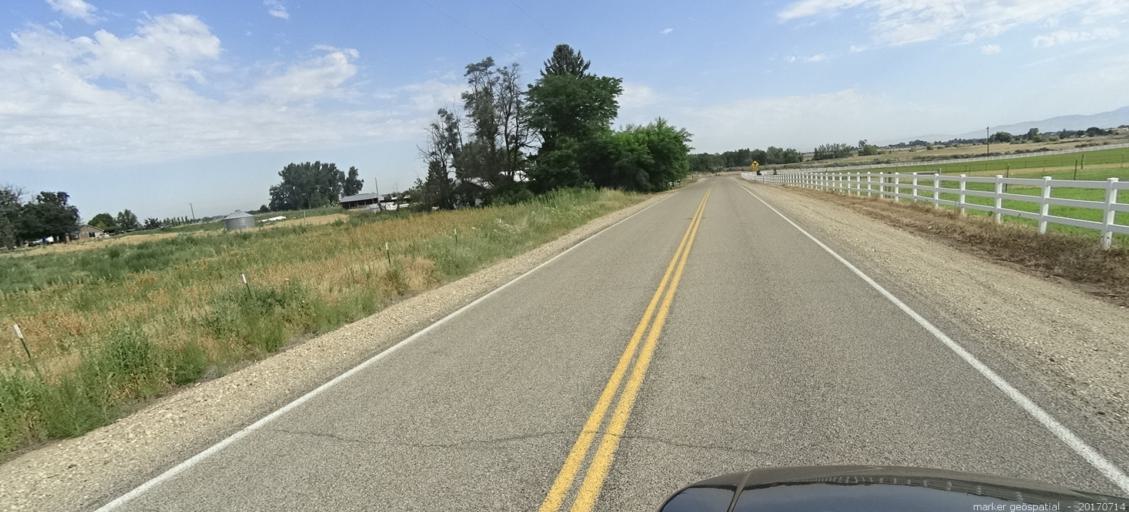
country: US
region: Idaho
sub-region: Ada County
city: Kuna
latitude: 43.5007
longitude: -116.3543
